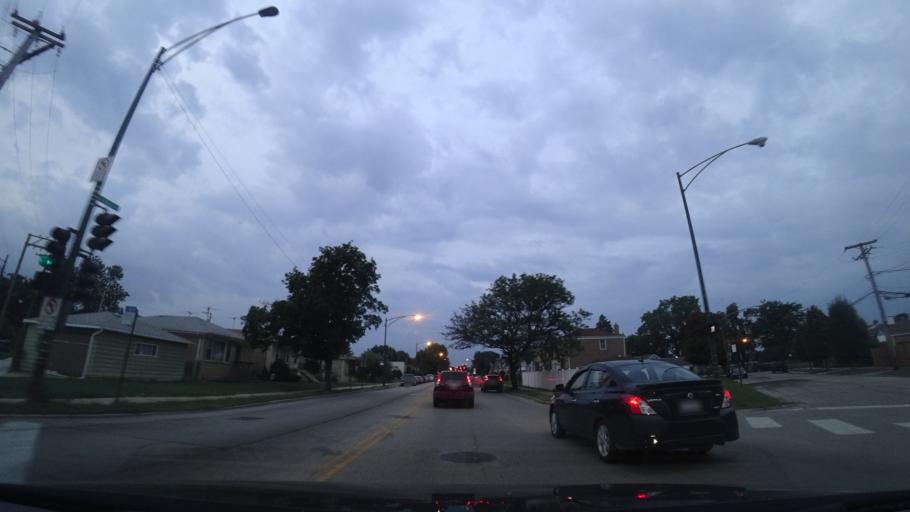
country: US
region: Illinois
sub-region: Cook County
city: Harwood Heights
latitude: 41.9851
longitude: -87.7877
